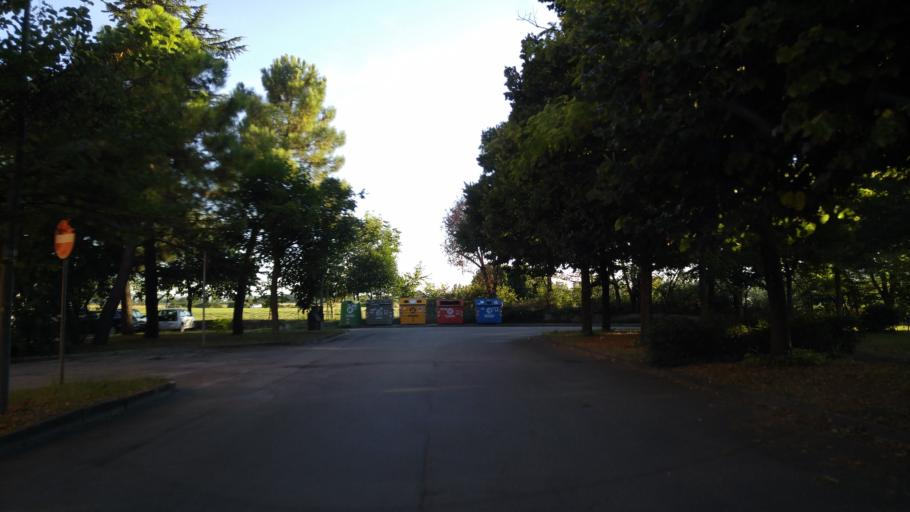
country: IT
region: The Marches
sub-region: Provincia di Pesaro e Urbino
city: Fano
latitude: 43.8300
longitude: 13.0216
